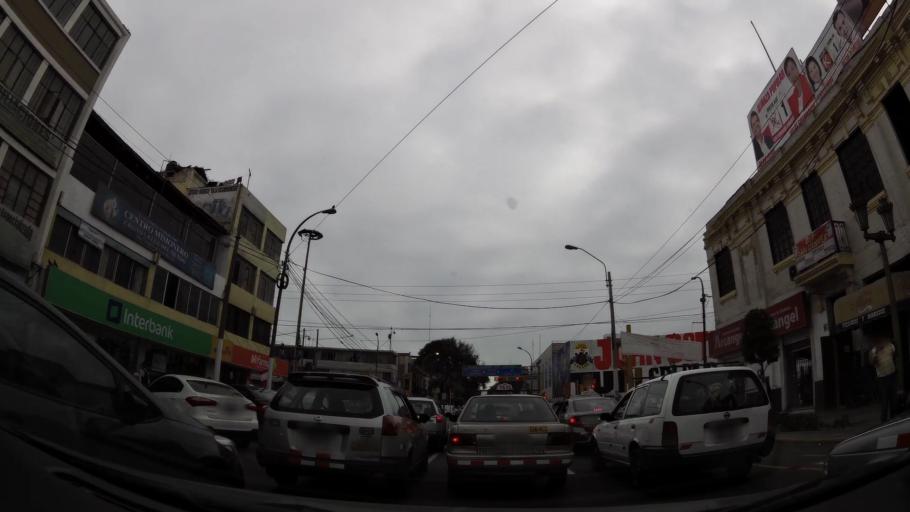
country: PE
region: Callao
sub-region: Callao
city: Callao
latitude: -12.0609
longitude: -77.1426
